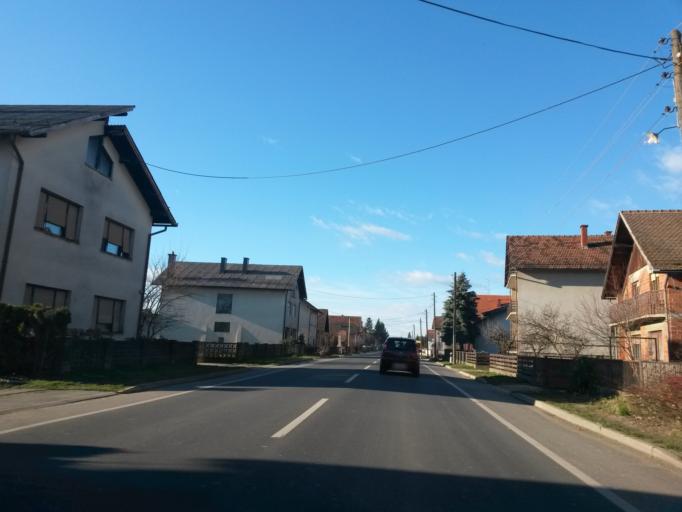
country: HR
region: Varazdinska
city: Tuzno
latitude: 46.2858
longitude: 16.2432
